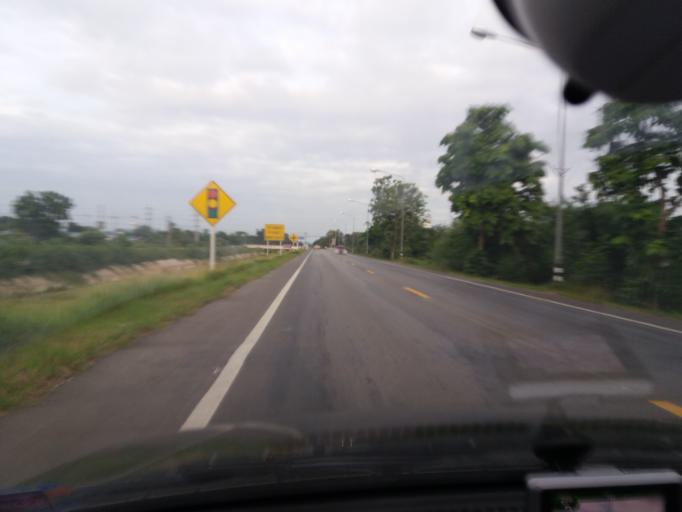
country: TH
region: Suphan Buri
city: U Thong
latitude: 14.5137
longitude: 99.9173
